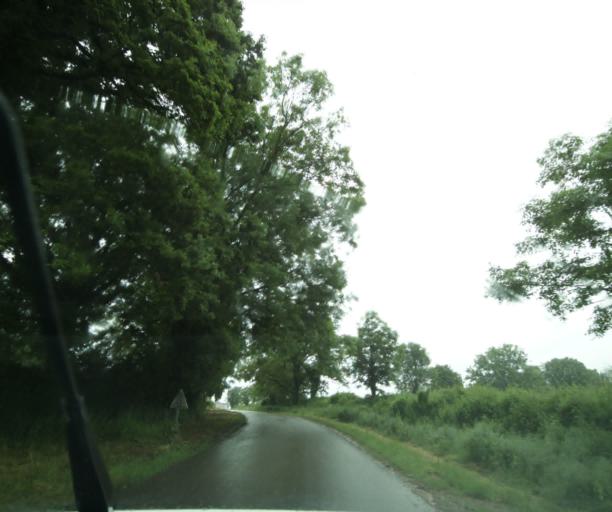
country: FR
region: Bourgogne
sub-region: Departement de Saone-et-Loire
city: Charolles
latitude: 46.4069
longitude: 4.2539
